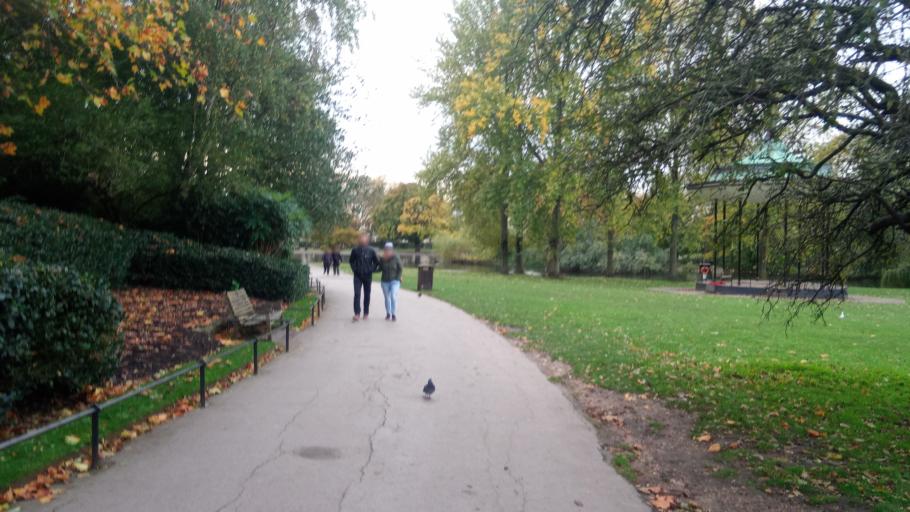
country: GB
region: England
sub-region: Greater London
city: Camden Town
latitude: 51.5264
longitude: -0.1569
